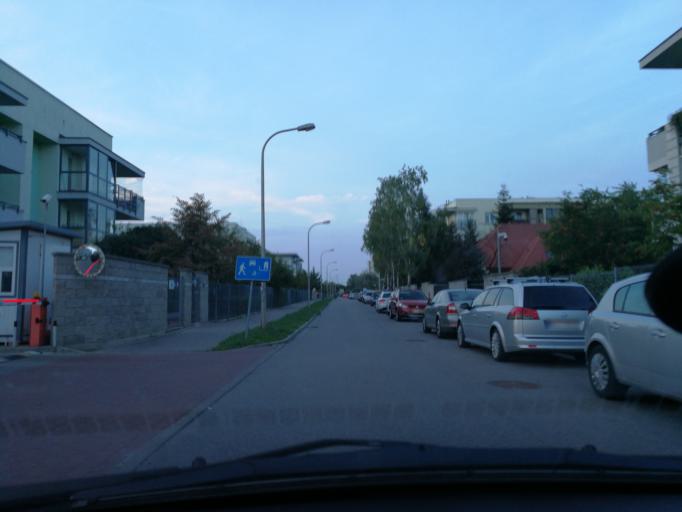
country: PL
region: Masovian Voivodeship
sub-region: Warszawa
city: Bemowo
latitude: 52.2367
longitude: 20.8936
